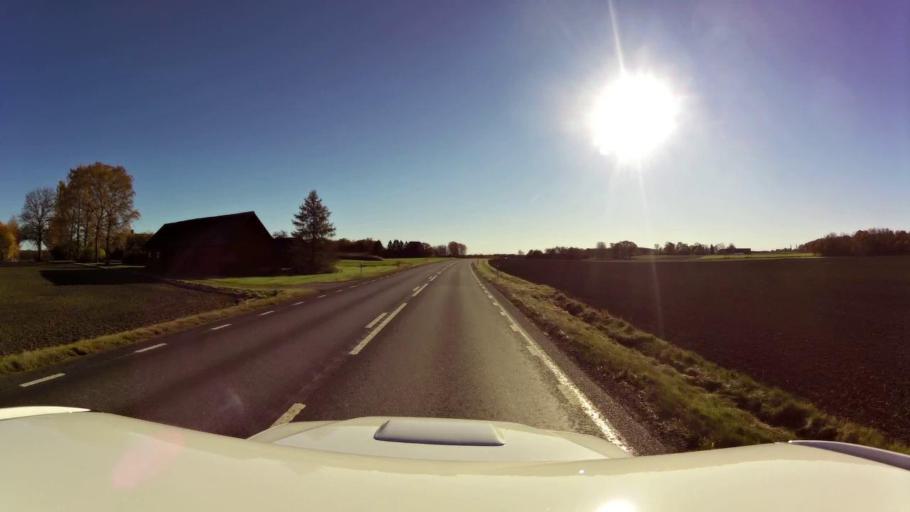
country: SE
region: OEstergoetland
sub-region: Linkopings Kommun
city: Ljungsbro
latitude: 58.5262
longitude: 15.4141
